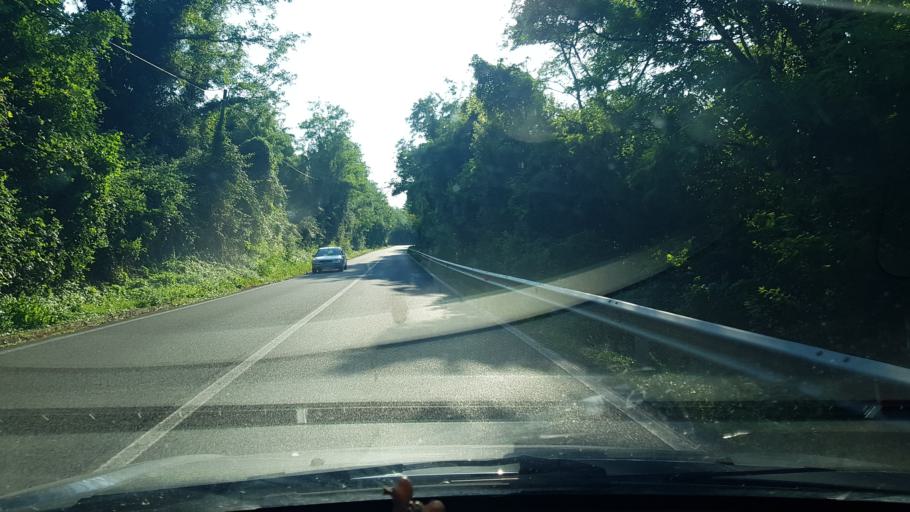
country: IT
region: Friuli Venezia Giulia
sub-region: Provincia di Gorizia
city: Farra d'Isonzo
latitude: 45.8926
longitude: 13.5298
